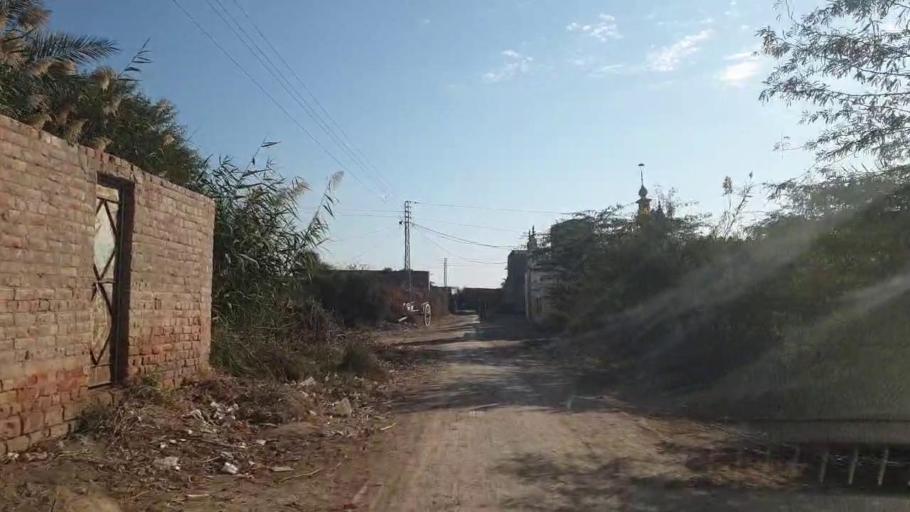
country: PK
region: Sindh
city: Sinjhoro
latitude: 26.0756
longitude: 68.8689
